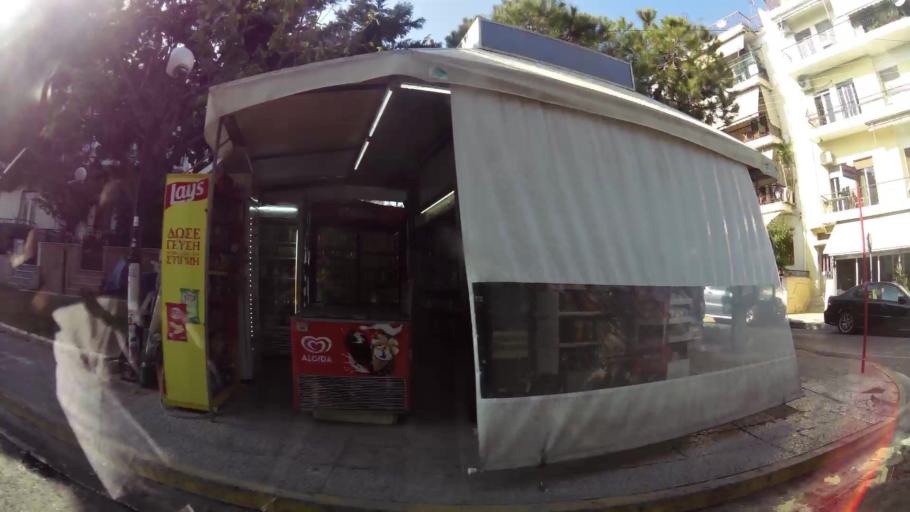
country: GR
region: Attica
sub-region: Nomos Piraios
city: Keratsini
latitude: 37.9637
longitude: 23.6261
